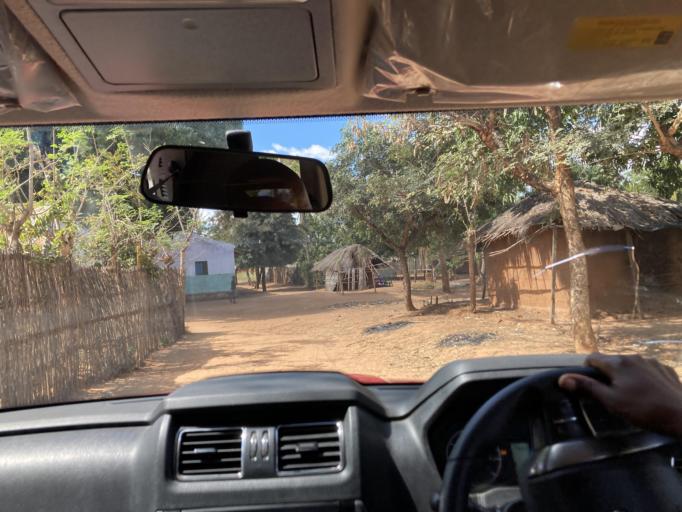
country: MZ
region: Cabo Delgado
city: Montepuez
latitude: -13.1448
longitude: 38.9834
